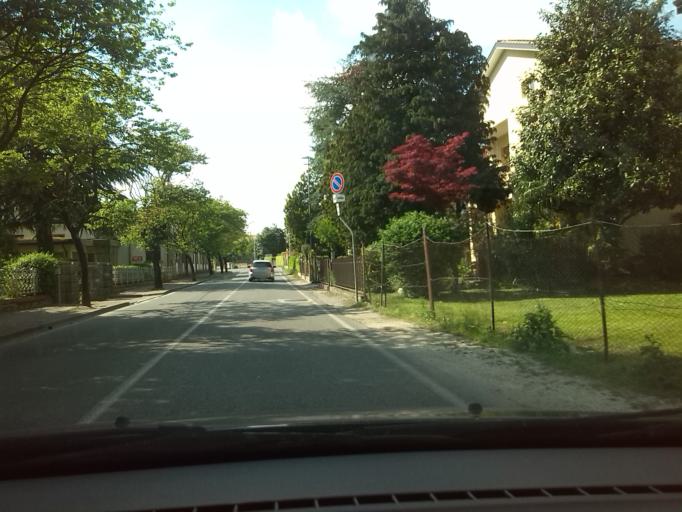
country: IT
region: Friuli Venezia Giulia
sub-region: Provincia di Udine
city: Cividale del Friuli
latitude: 46.0987
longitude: 13.4226
